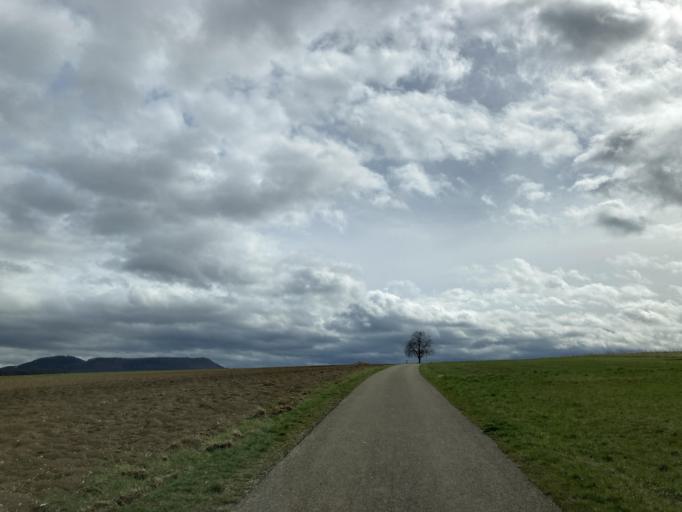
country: DE
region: Baden-Wuerttemberg
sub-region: Tuebingen Region
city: Gomaringen
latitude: 48.4675
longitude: 9.0998
